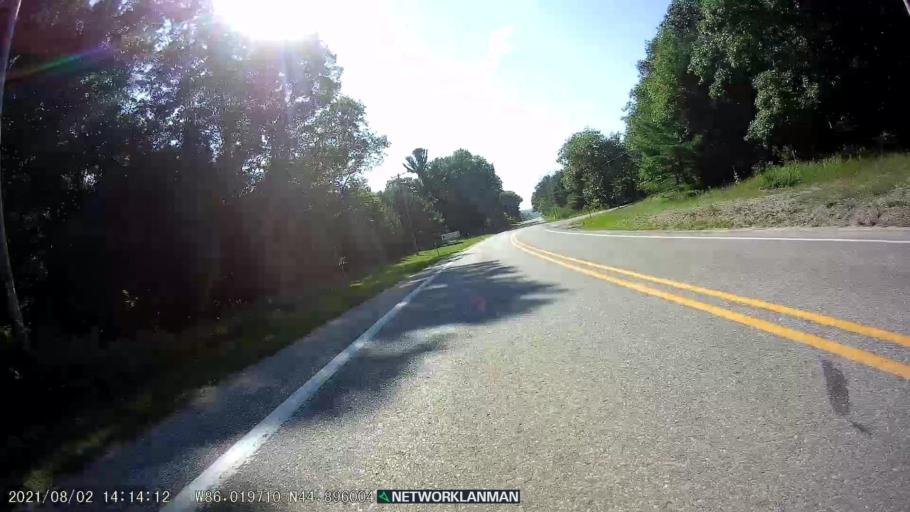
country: US
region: Michigan
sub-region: Benzie County
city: Beulah
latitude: 44.8952
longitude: -86.0179
